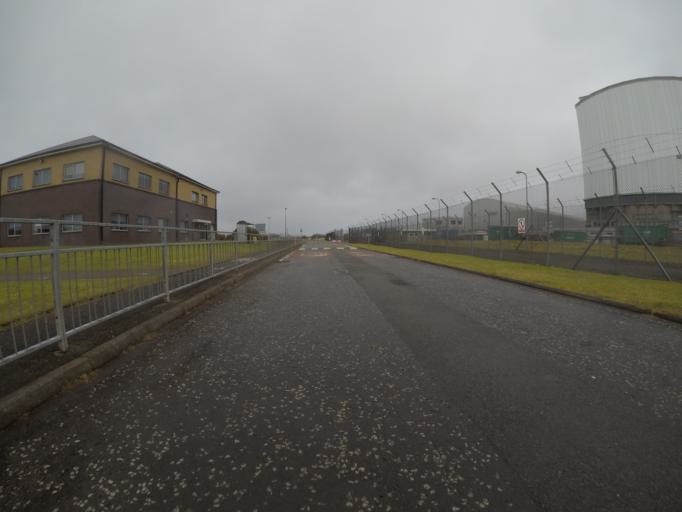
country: GB
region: Scotland
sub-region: North Ayrshire
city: Millport
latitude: 55.7195
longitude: -4.8999
